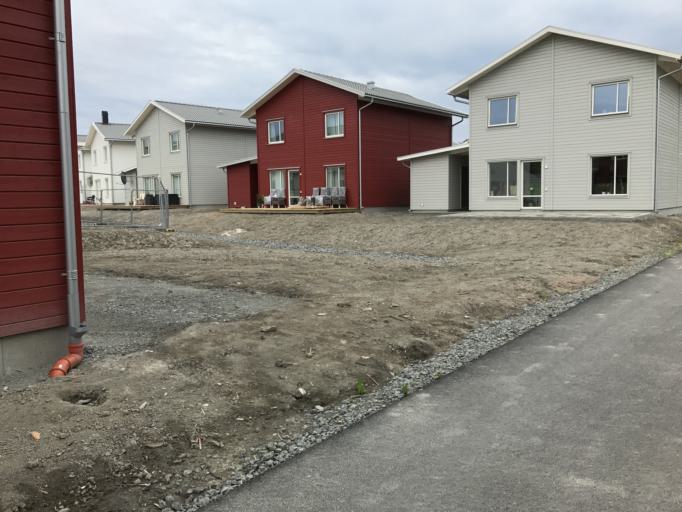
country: SE
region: Vaestra Goetaland
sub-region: Goteborg
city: Majorna
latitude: 57.7345
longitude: 11.8873
